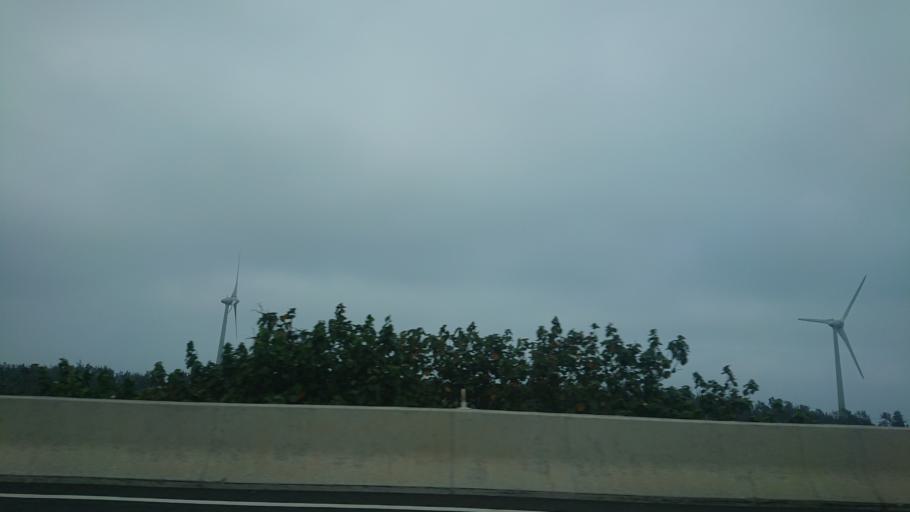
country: TW
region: Taiwan
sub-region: Miaoli
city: Miaoli
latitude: 24.5015
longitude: 120.6787
